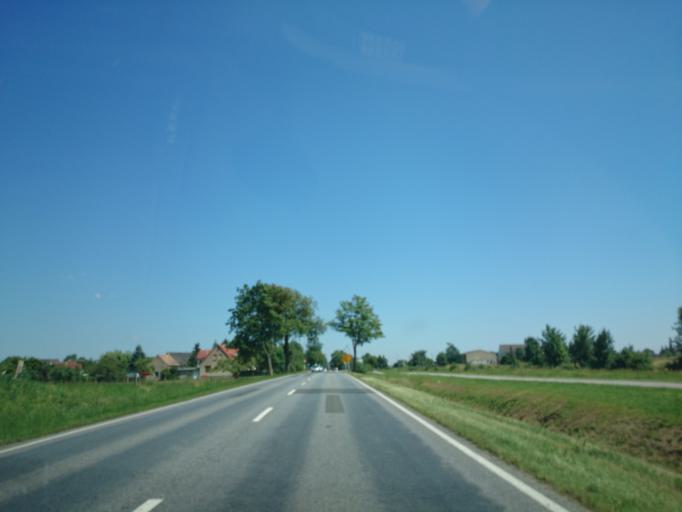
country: DE
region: Mecklenburg-Vorpommern
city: Broderstorf
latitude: 54.0794
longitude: 12.2557
